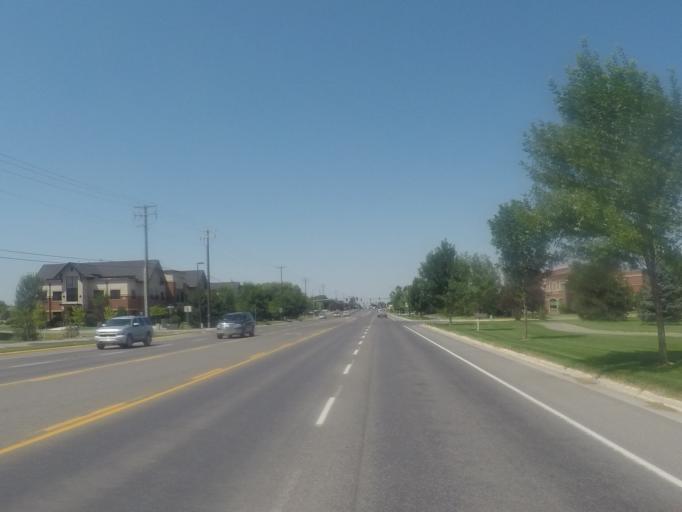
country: US
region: Montana
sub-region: Gallatin County
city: Bozeman
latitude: 45.6931
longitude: -111.0540
